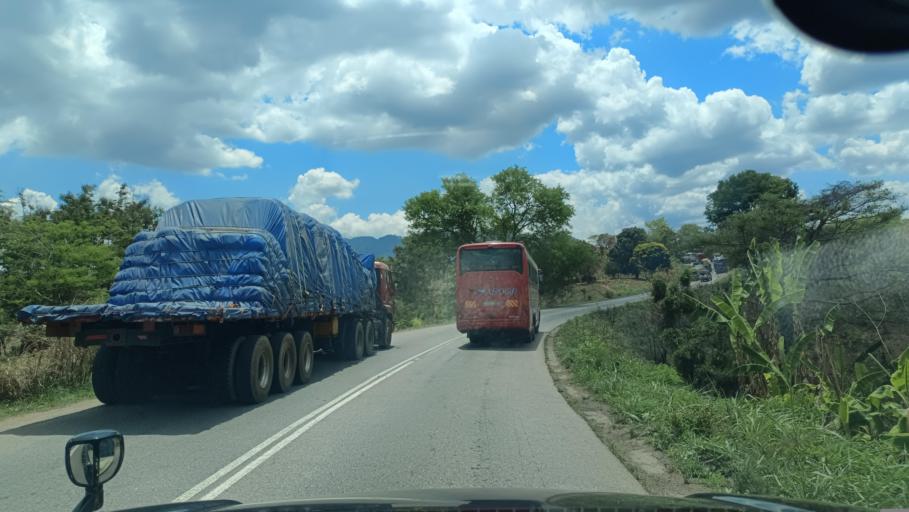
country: TZ
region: Morogoro
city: Mikumi
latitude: -7.4650
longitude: 36.9186
